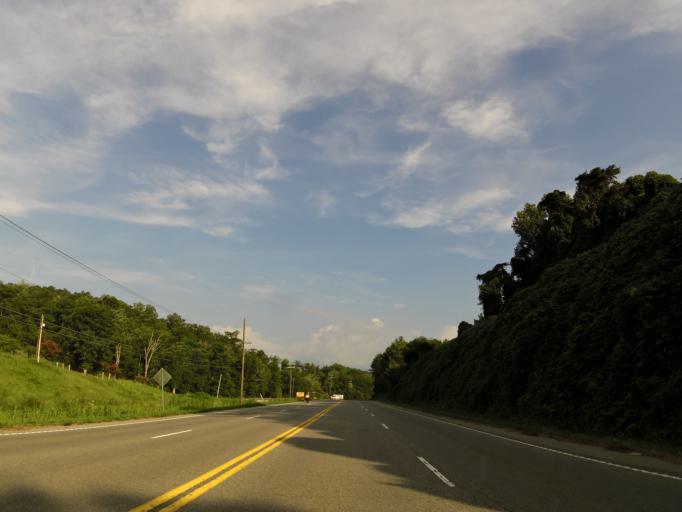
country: US
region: Tennessee
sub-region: Sevier County
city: Seymour
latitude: 35.8645
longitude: -83.6570
